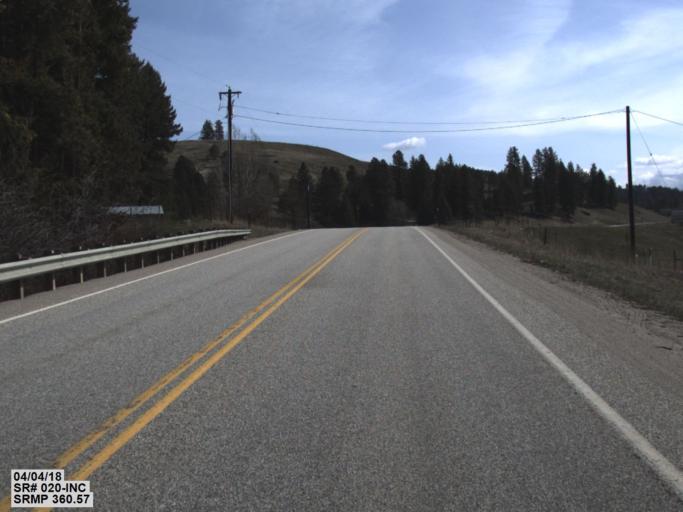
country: US
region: Washington
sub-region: Stevens County
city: Colville
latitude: 48.5153
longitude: -117.7973
